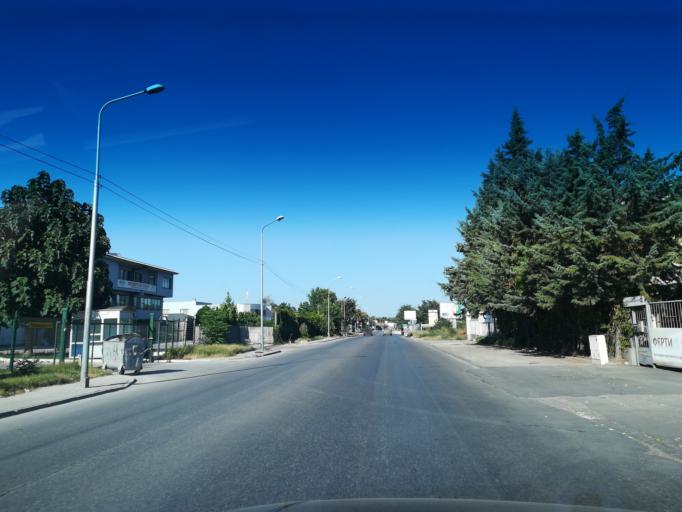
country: BG
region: Plovdiv
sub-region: Obshtina Plovdiv
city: Plovdiv
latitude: 42.1616
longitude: 24.7686
